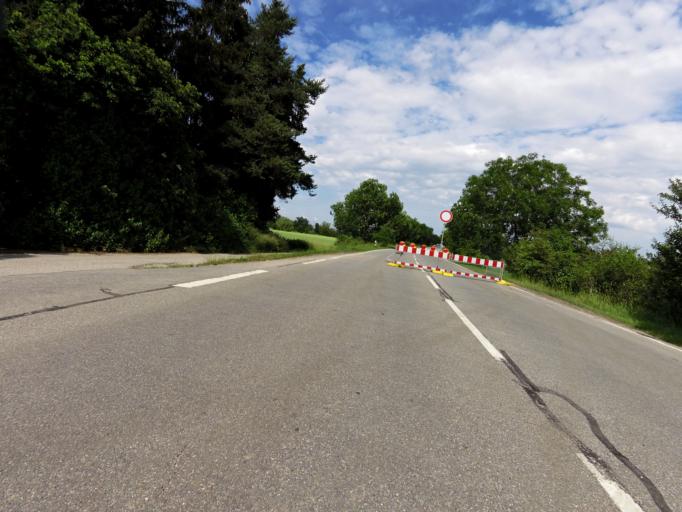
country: DE
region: Bavaria
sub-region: Upper Bavaria
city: Moosburg
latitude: 48.4730
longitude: 11.9657
